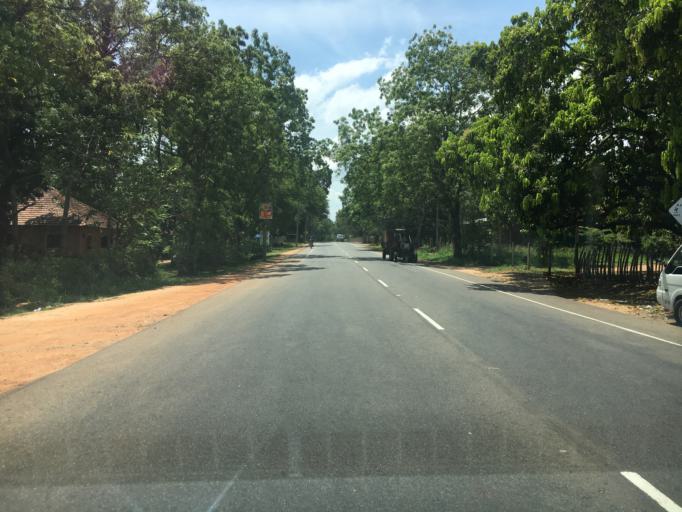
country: LK
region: North Central
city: Anuradhapura
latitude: 8.2691
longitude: 80.5030
